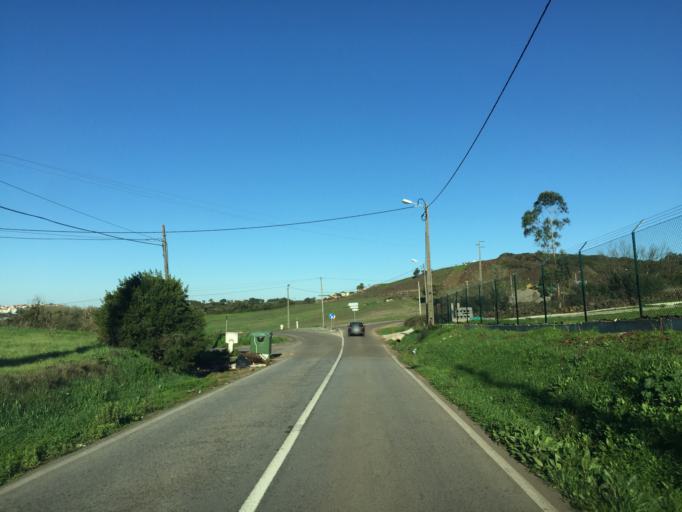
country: PT
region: Lisbon
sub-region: Sintra
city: Almargem
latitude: 38.8698
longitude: -9.2857
